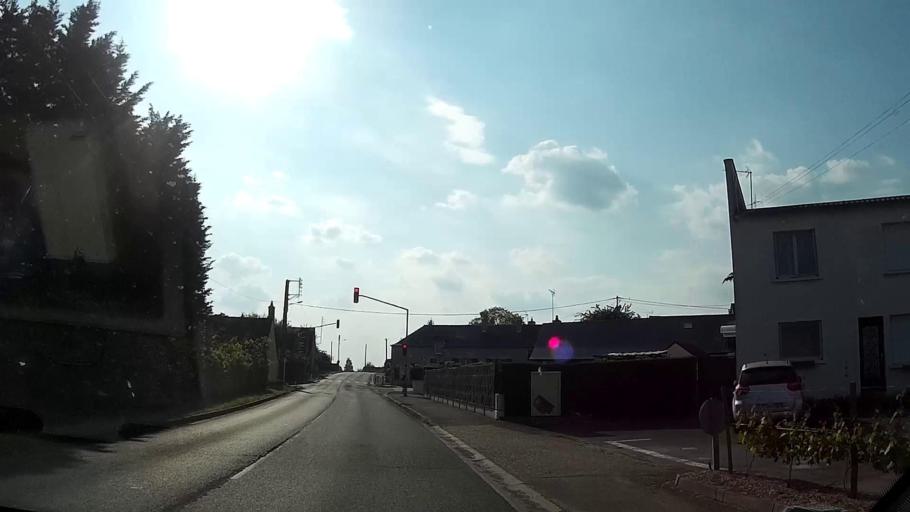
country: FR
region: Centre
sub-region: Departement du Loir-et-Cher
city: Saint-Sulpice-de-Pommeray
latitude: 47.6073
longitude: 1.2739
